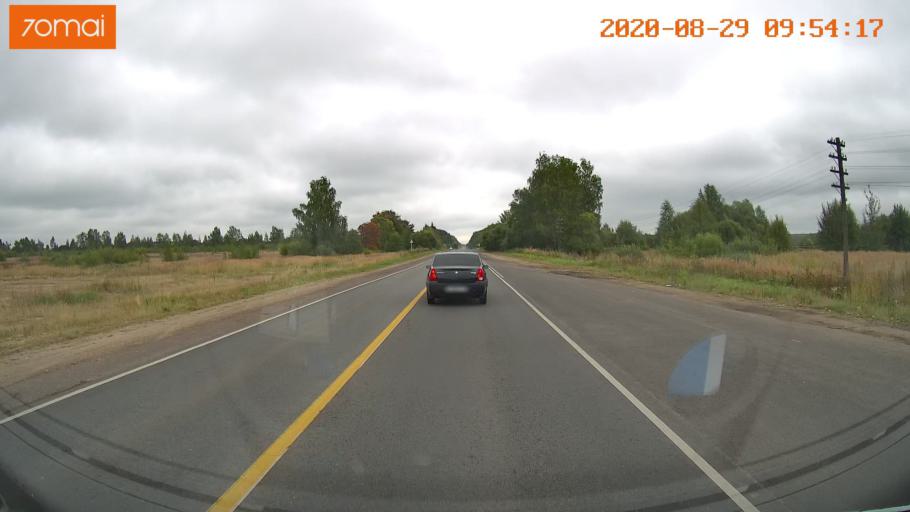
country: RU
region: Ivanovo
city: Zarechnyy
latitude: 57.4238
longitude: 42.2375
